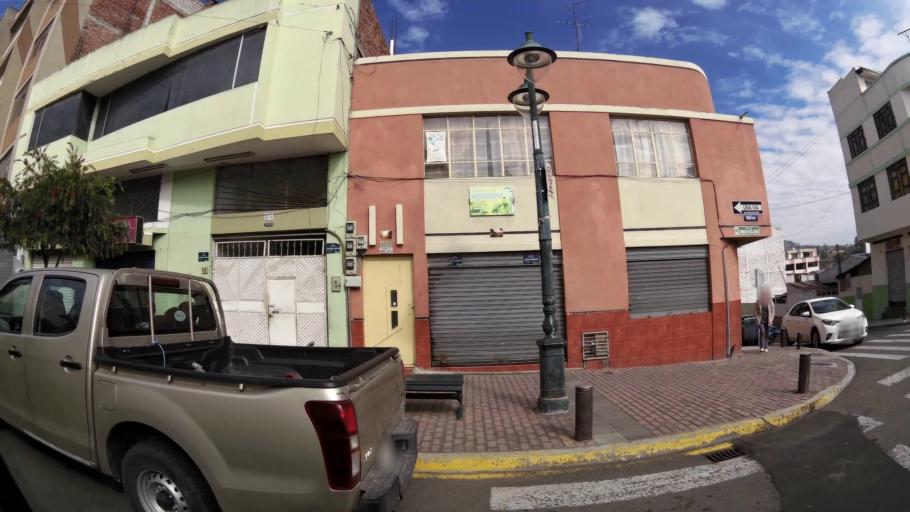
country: EC
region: Tungurahua
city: Ambato
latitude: -1.2527
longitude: -78.6433
